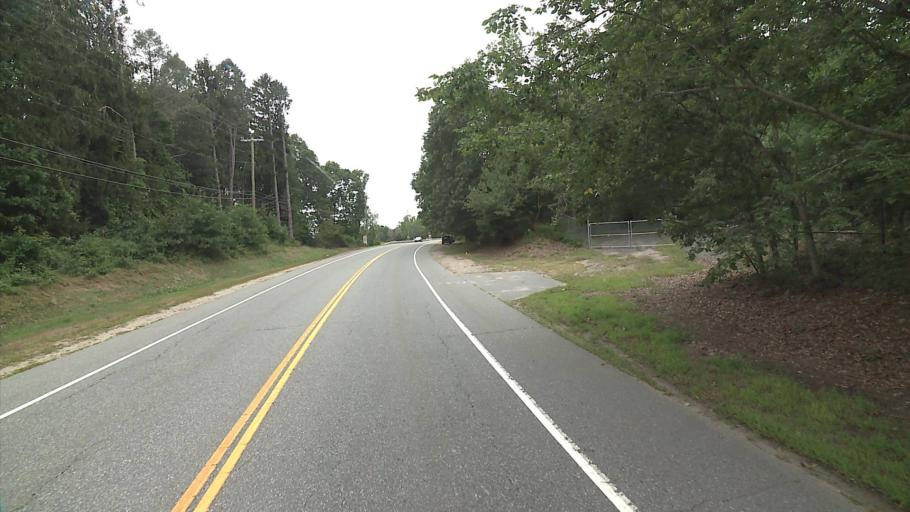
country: US
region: Connecticut
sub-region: Middlesex County
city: Old Saybrook Center
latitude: 41.2883
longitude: -72.3111
